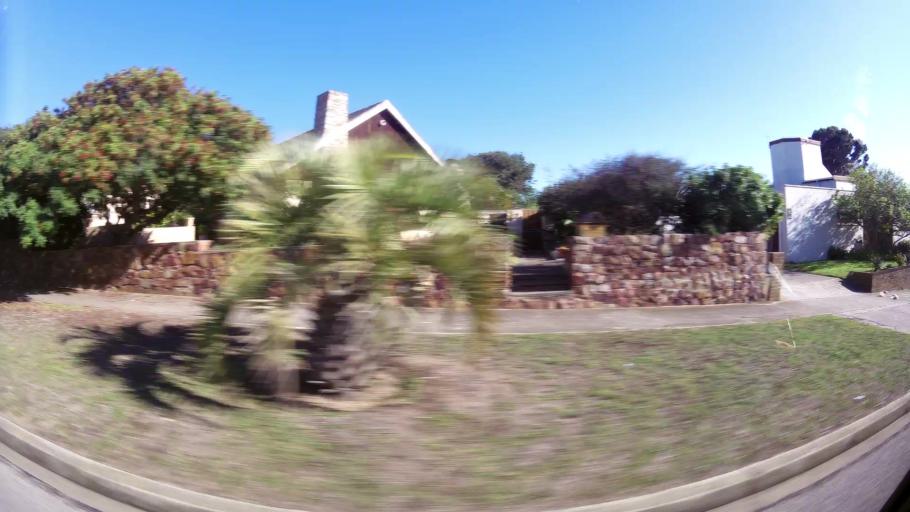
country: ZA
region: Eastern Cape
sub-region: Nelson Mandela Bay Metropolitan Municipality
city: Port Elizabeth
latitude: -33.9771
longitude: 25.6355
